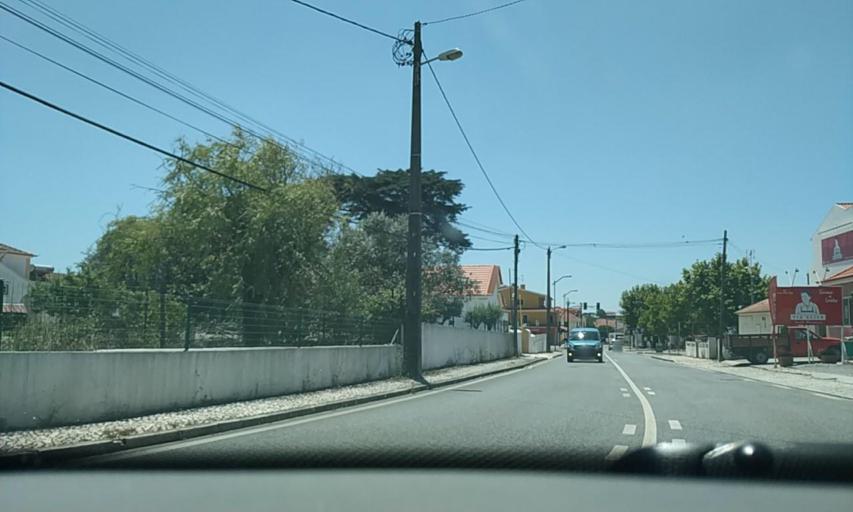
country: PT
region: Lisbon
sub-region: Sintra
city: Almargem
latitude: 38.8793
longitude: -9.2766
